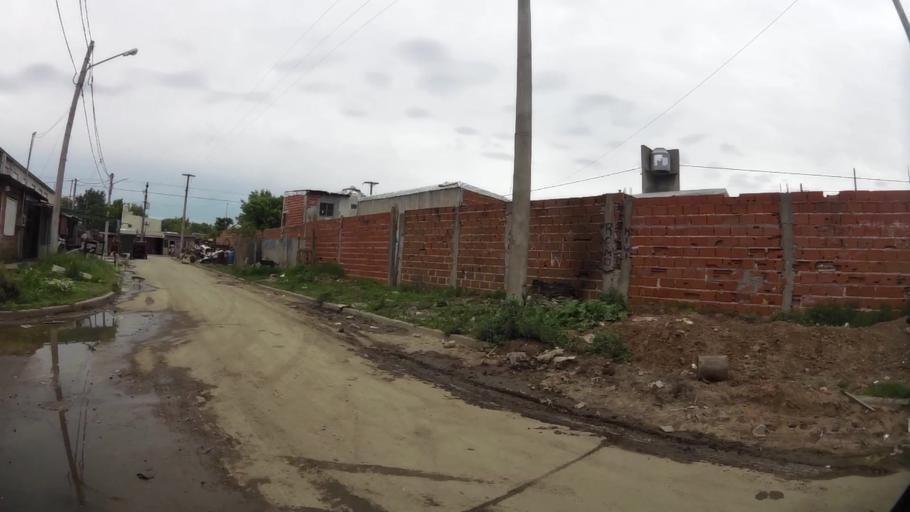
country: AR
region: Buenos Aires
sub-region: Partido de Campana
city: Campana
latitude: -34.1852
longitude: -58.9360
